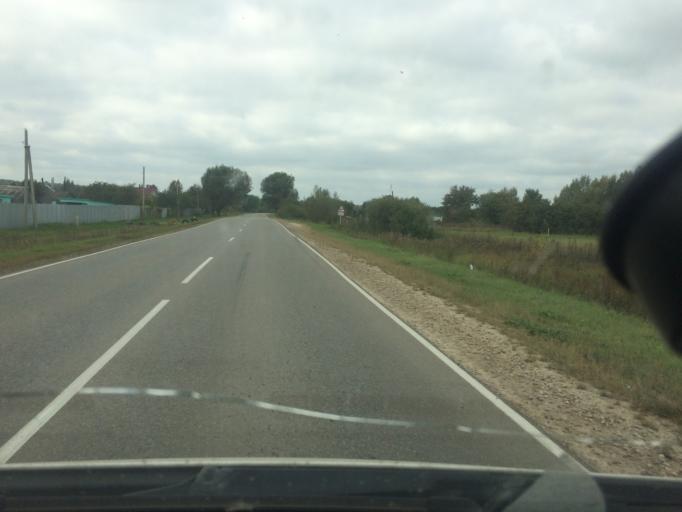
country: RU
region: Tula
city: Odoyev
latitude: 53.9986
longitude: 36.6762
